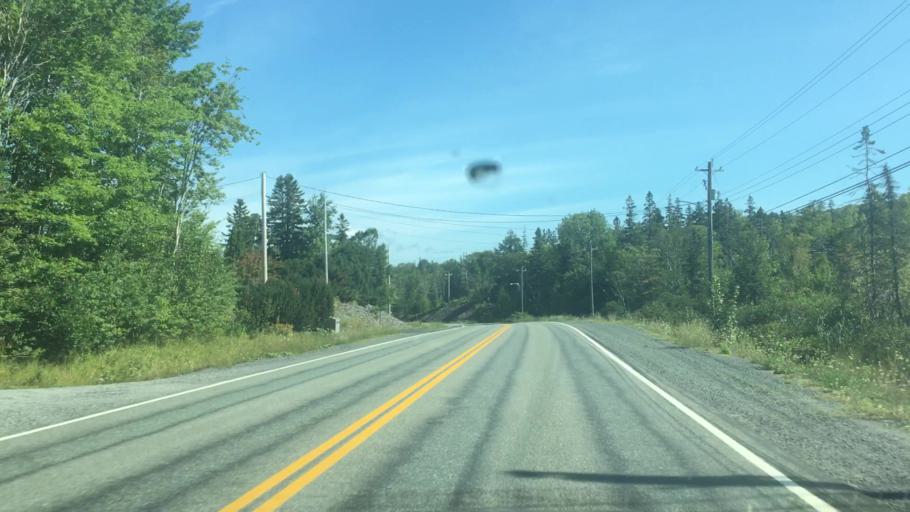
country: CA
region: Nova Scotia
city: Sydney
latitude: 45.9964
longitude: -60.4053
